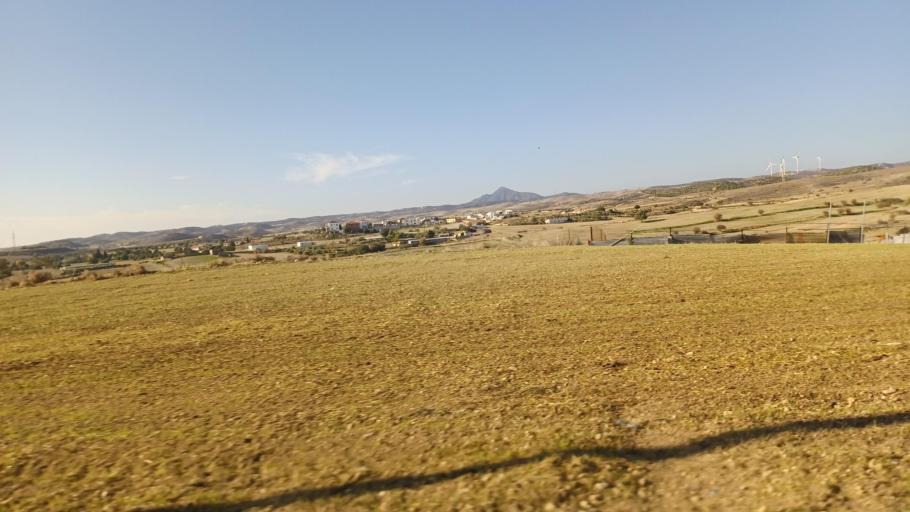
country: CY
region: Larnaka
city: Aradippou
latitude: 34.9344
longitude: 33.5307
